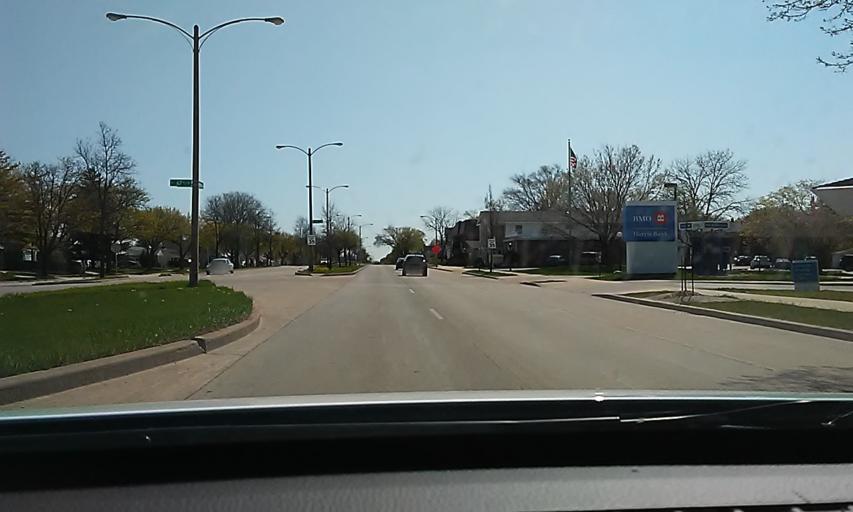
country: US
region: Wisconsin
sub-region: Milwaukee County
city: West Allis
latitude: 42.9883
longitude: -87.9971
